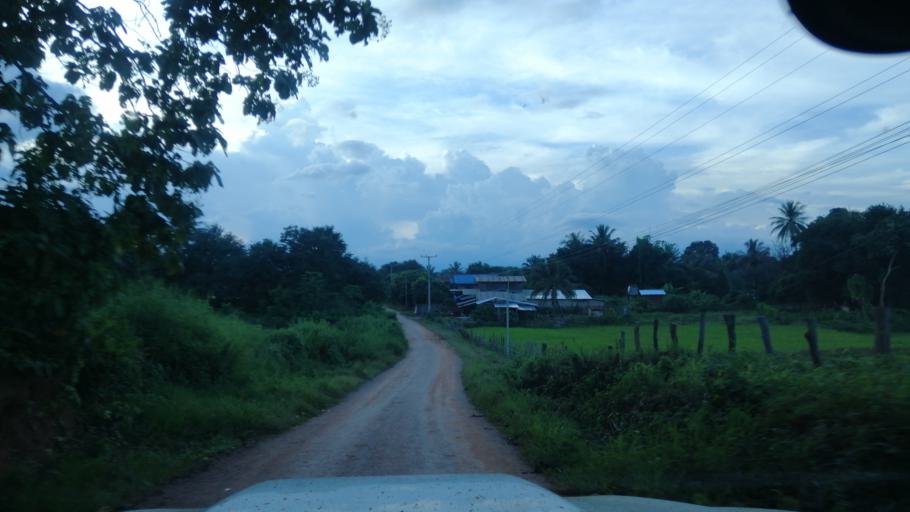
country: TH
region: Uttaradit
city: Ban Khok
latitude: 17.8691
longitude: 101.0929
